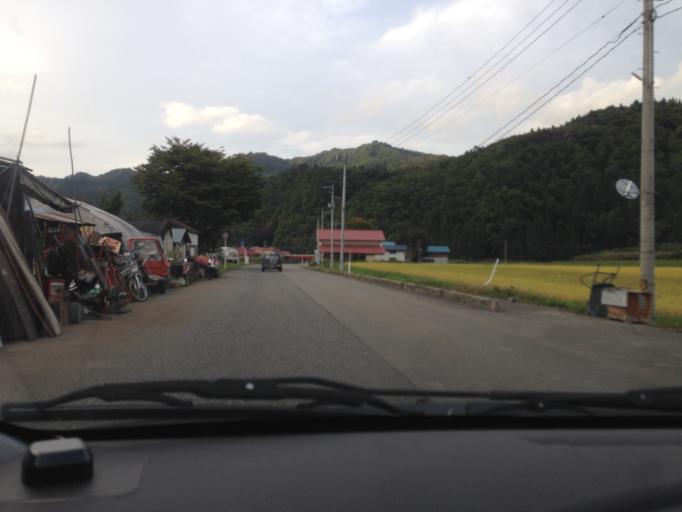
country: JP
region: Fukushima
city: Kitakata
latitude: 37.3587
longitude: 139.5756
